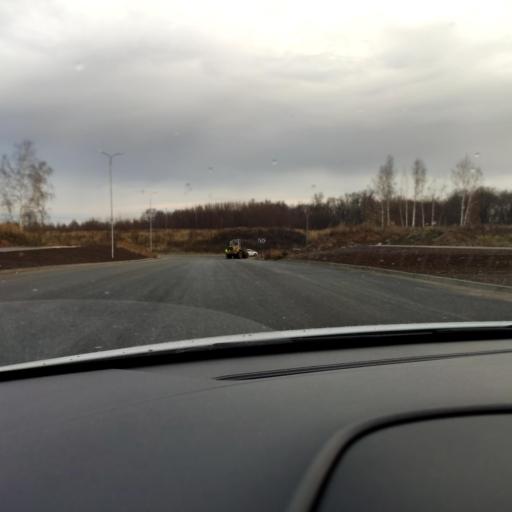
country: RU
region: Tatarstan
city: Osinovo
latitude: 55.8626
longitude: 48.8981
